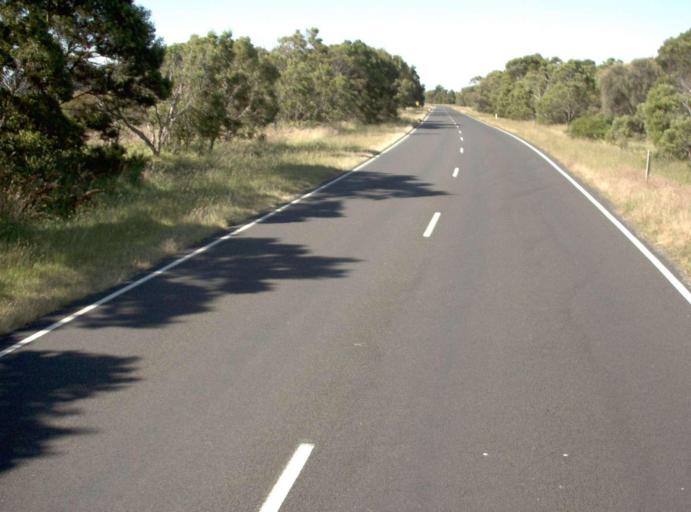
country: AU
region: Victoria
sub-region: Latrobe
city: Traralgon
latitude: -38.6334
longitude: 146.6757
